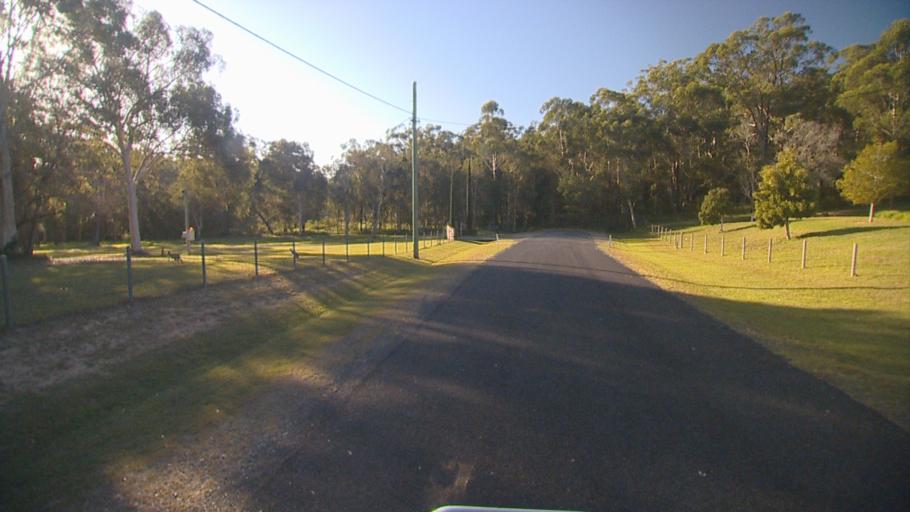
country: AU
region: Queensland
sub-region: Redland
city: Redland Bay
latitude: -27.6574
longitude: 153.2671
